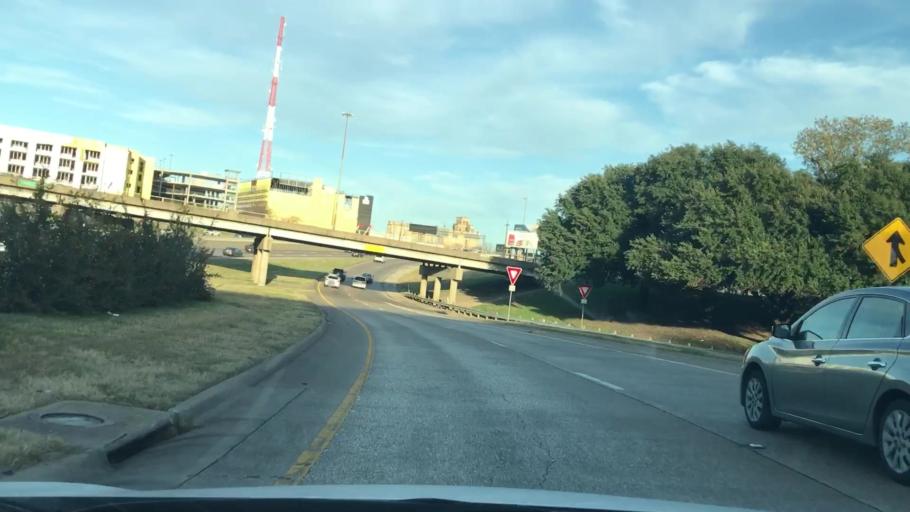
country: US
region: Texas
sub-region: Dallas County
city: Dallas
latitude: 32.7790
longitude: -96.7808
